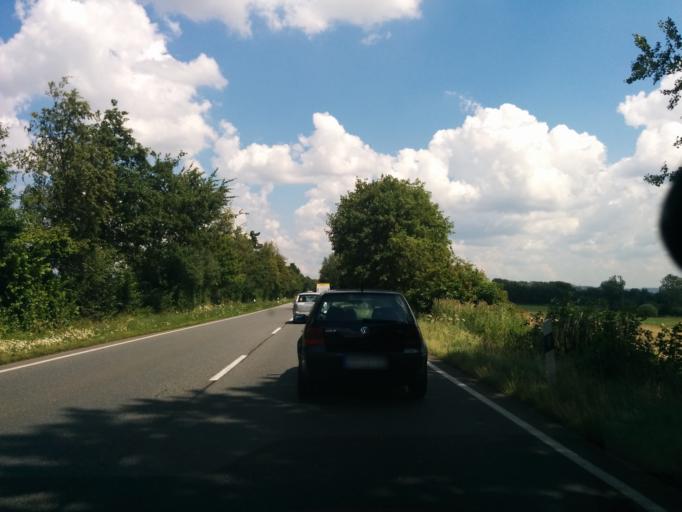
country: DE
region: Lower Saxony
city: Krebeck
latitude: 51.5767
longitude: 10.1280
